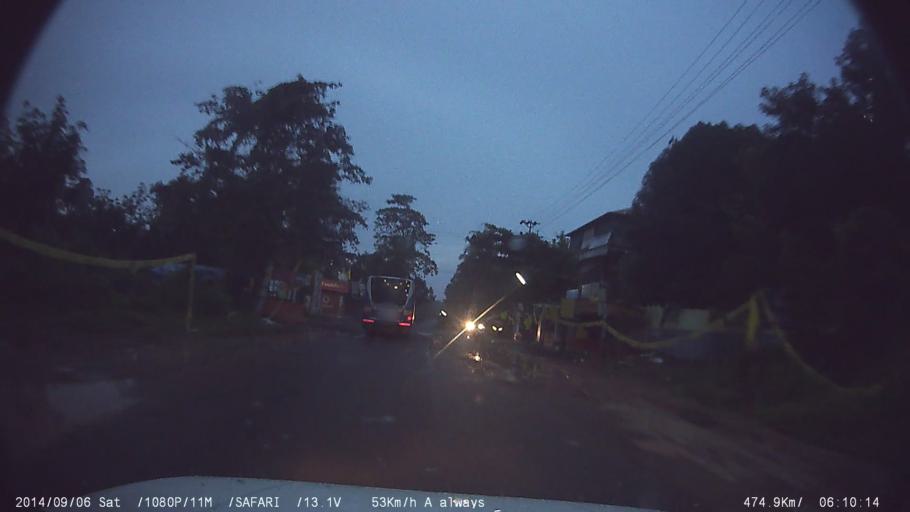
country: IN
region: Kerala
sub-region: Alappuzha
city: Arukutti
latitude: 9.9142
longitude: 76.3877
